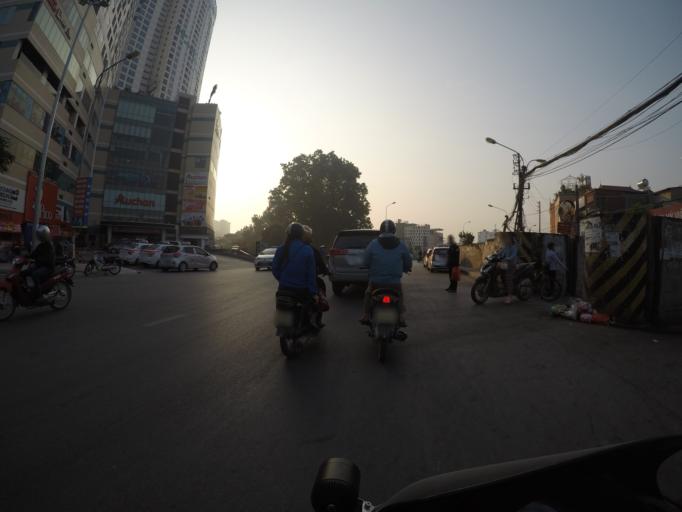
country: VN
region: Ha Noi
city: Hoan Kiem
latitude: 21.0455
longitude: 105.8655
